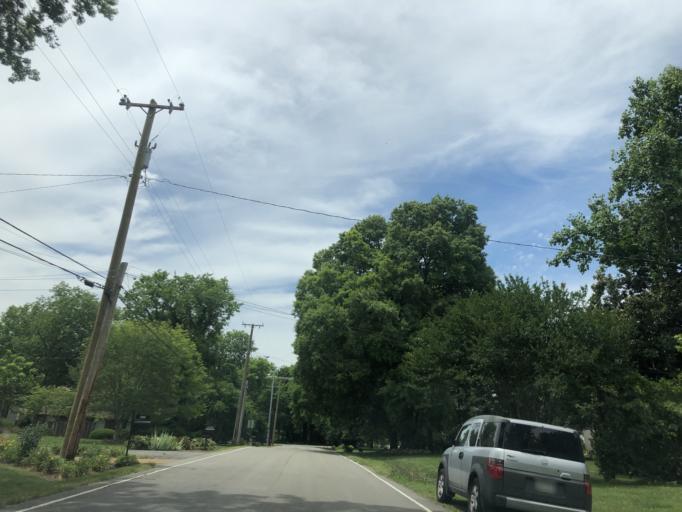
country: US
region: Tennessee
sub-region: Davidson County
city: Oak Hill
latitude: 36.1117
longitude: -86.7986
